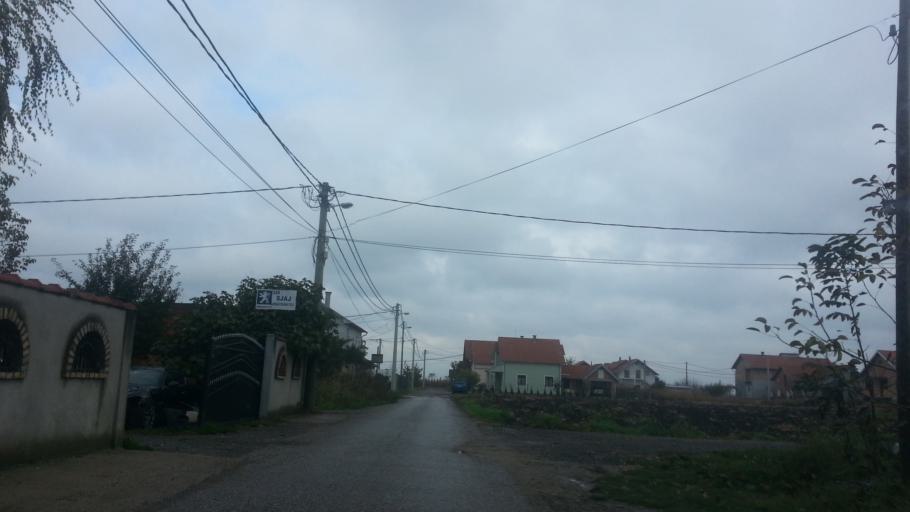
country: RS
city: Novi Banovci
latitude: 44.9139
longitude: 20.2880
